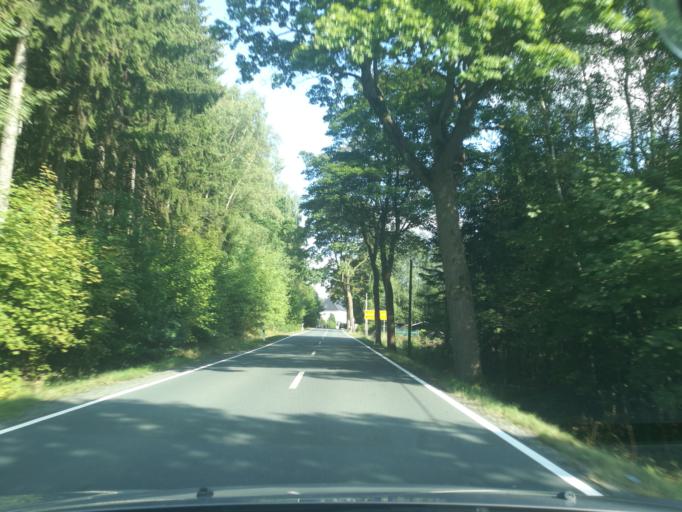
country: CZ
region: Karlovarsky
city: Hranice
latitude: 50.3229
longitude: 12.1627
